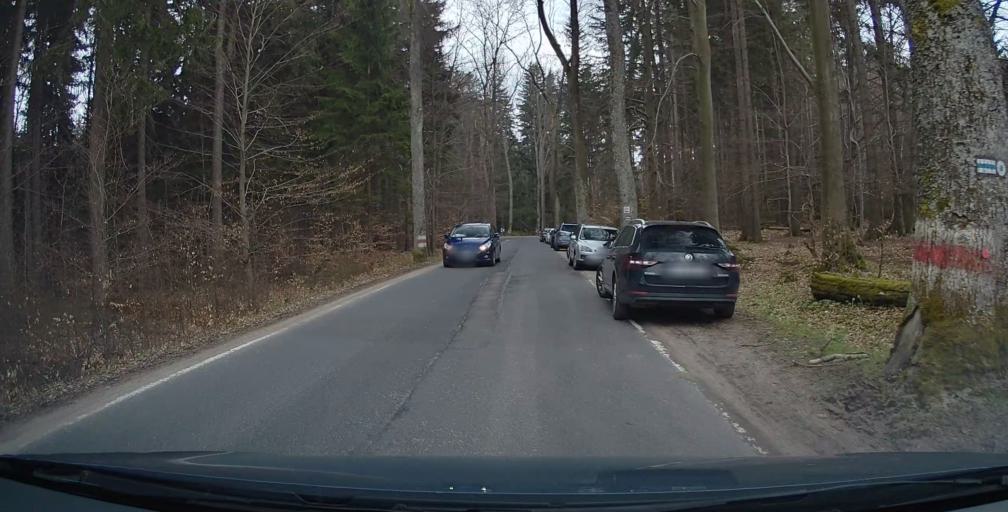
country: PL
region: Lower Silesian Voivodeship
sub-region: Powiat klodzki
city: Radkow
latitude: 50.4759
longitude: 16.3874
